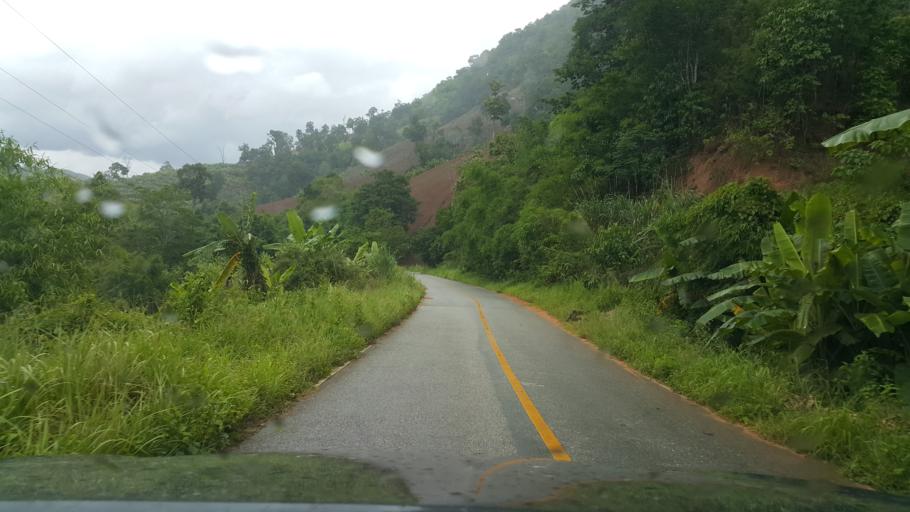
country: TH
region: Loei
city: Na Haeo
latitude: 17.5602
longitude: 100.8474
